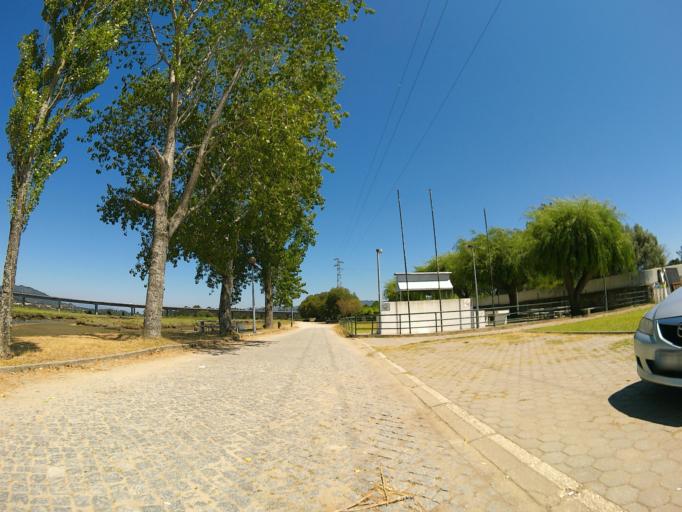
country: PT
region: Viana do Castelo
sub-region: Viana do Castelo
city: Darque
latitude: 41.6878
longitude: -8.7868
